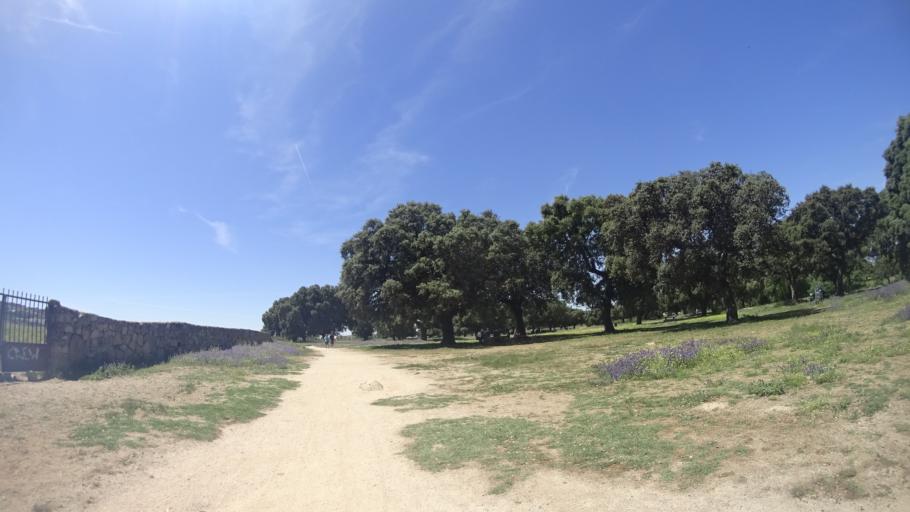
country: ES
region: Madrid
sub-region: Provincia de Madrid
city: Collado-Villalba
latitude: 40.6504
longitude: -4.0036
